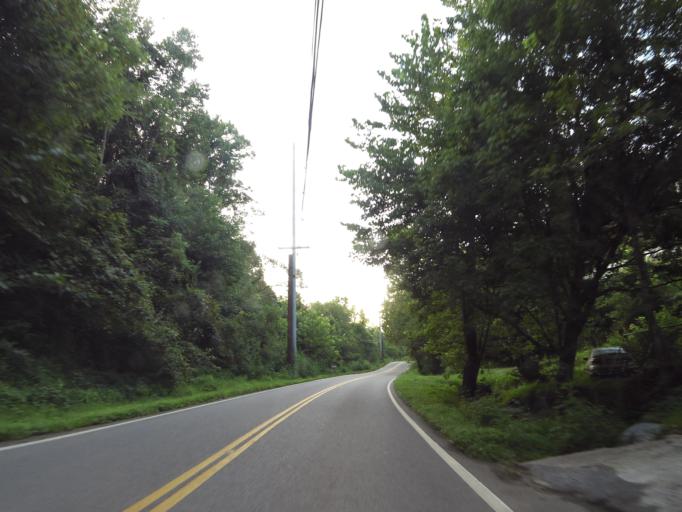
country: US
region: Tennessee
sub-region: Union County
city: Luttrell
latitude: 36.1916
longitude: -83.7434
